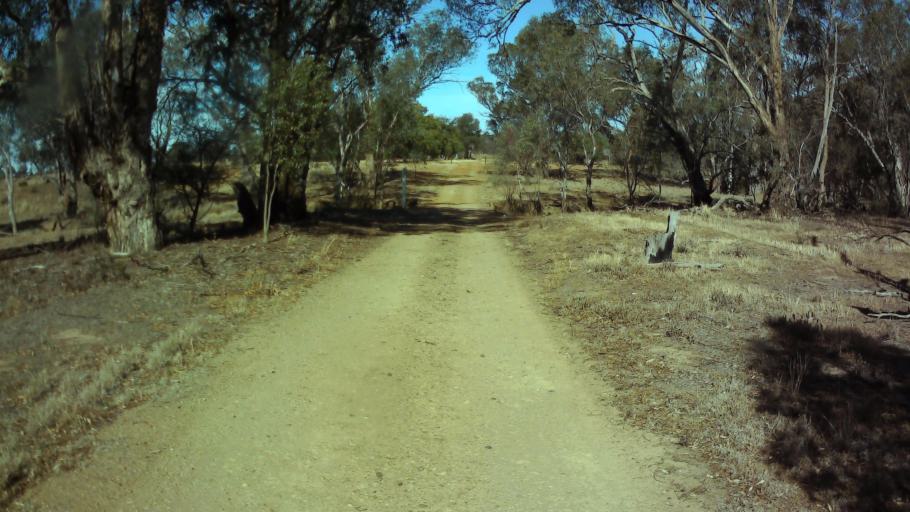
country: AU
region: New South Wales
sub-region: Weddin
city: Grenfell
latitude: -33.7336
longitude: 148.0931
